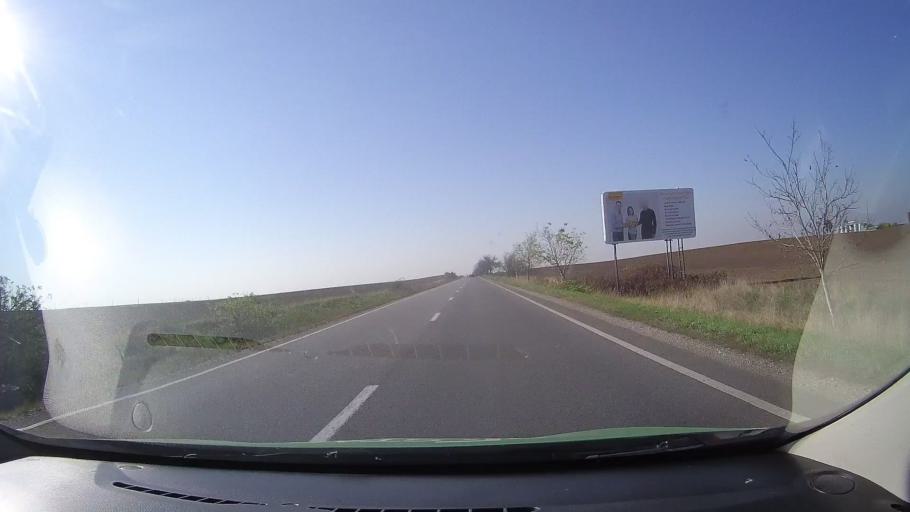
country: RO
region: Satu Mare
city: Carei
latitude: 47.6639
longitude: 22.4328
